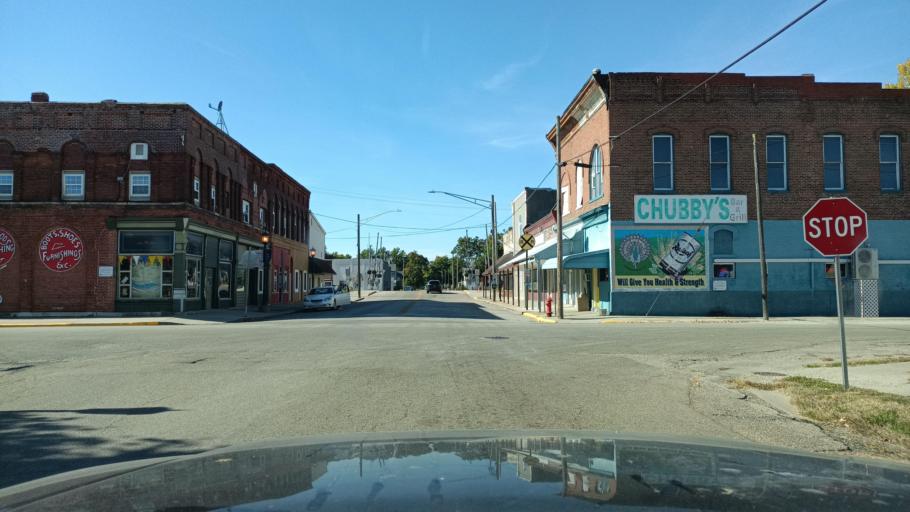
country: US
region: Illinois
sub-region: Logan County
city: Atlanta
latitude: 40.2609
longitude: -89.2309
